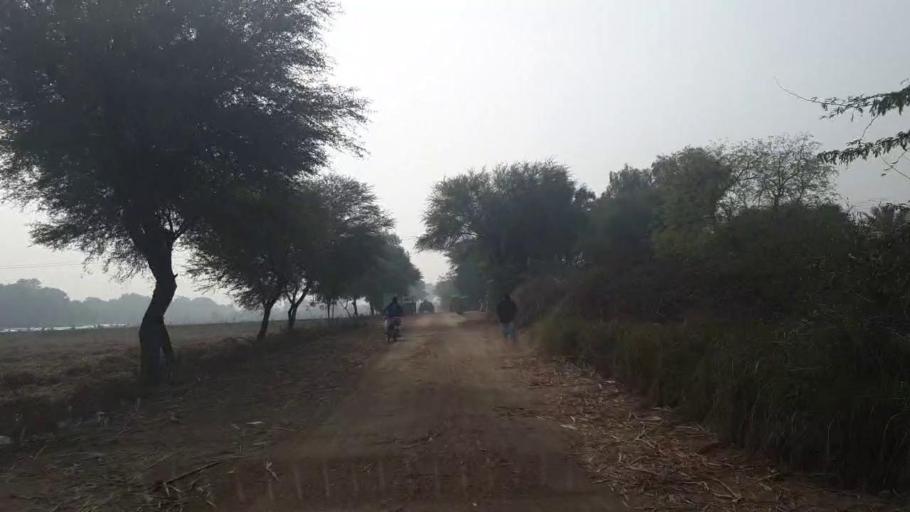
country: PK
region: Sindh
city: Tando Adam
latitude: 25.7687
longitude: 68.6073
